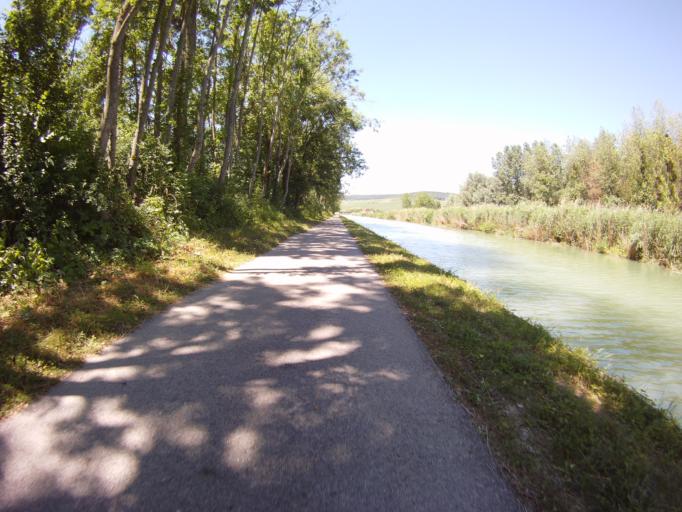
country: FR
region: Champagne-Ardenne
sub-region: Departement de la Marne
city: Dizy
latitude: 49.0638
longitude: 3.9550
